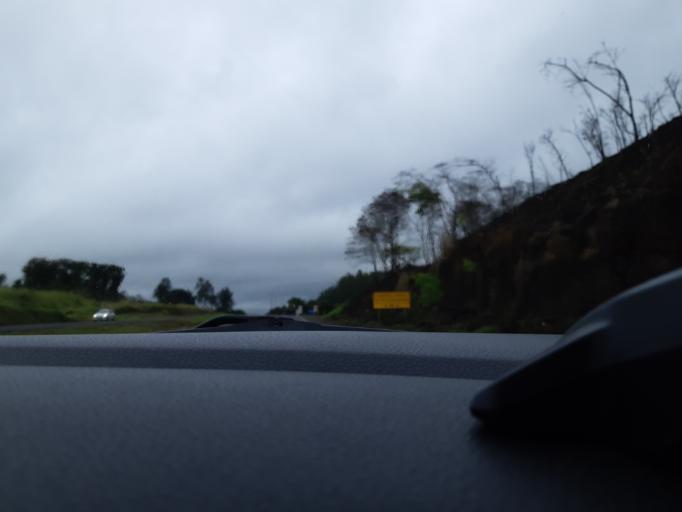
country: BR
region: Sao Paulo
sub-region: Ourinhos
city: Ourinhos
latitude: -22.9947
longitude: -49.9048
